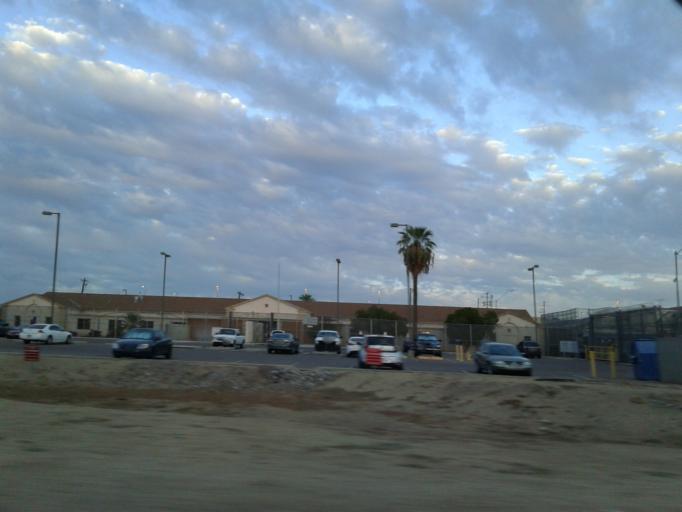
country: US
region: Arizona
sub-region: Maricopa County
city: Phoenix
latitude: 33.4530
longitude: -112.0301
